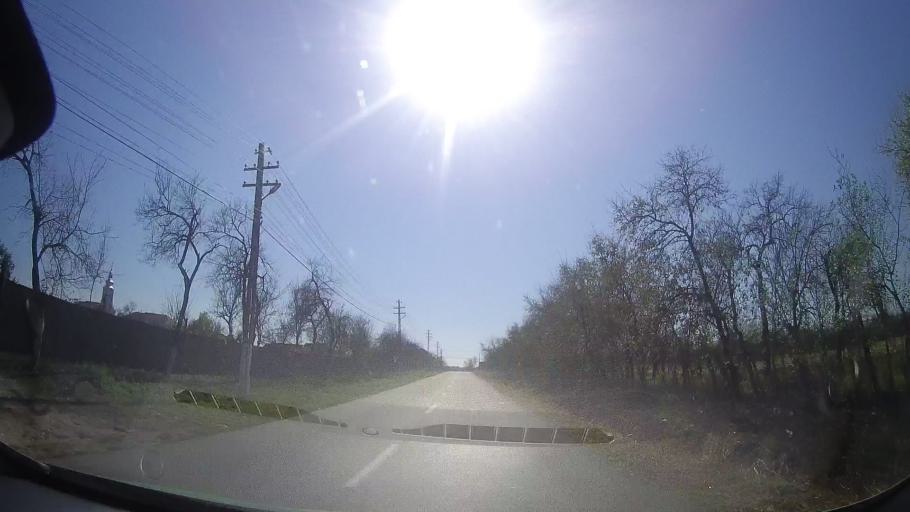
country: RO
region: Timis
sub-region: Comuna Bethausen
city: Bethausen
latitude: 45.7954
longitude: 21.9646
